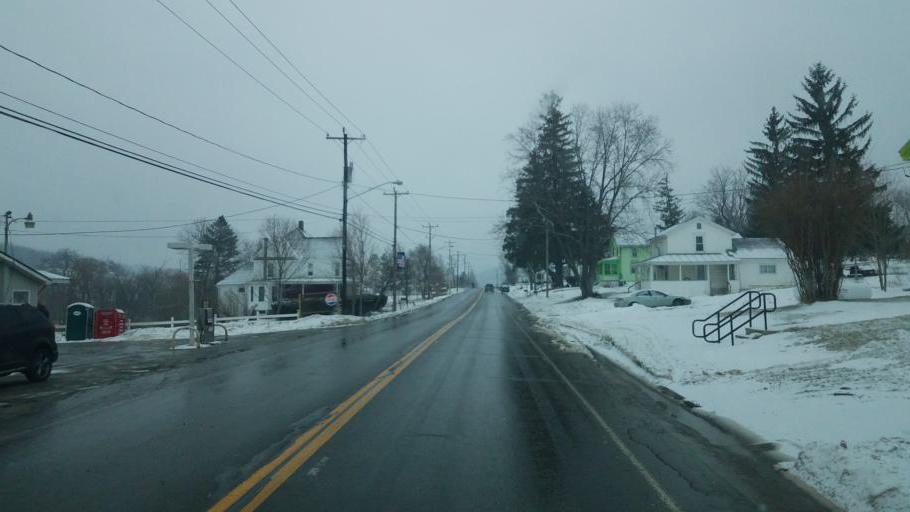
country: US
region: New York
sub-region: Steuben County
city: Canisteo
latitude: 42.1209
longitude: -77.5010
